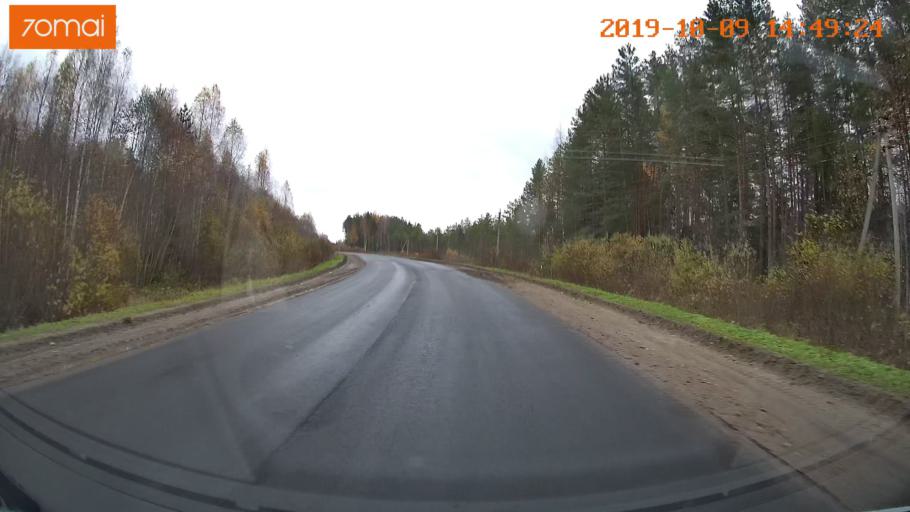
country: RU
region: Kostroma
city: Chistyye Bory
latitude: 58.3937
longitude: 41.5816
